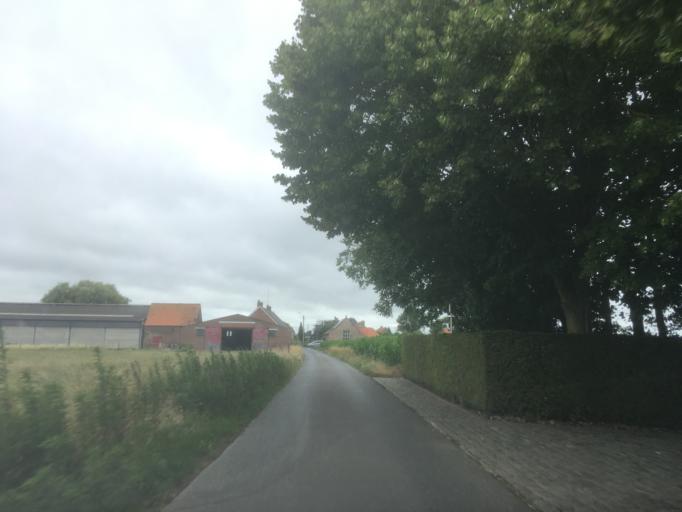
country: BE
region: Flanders
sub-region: Provincie West-Vlaanderen
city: Roeselare
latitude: 50.9186
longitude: 3.1060
